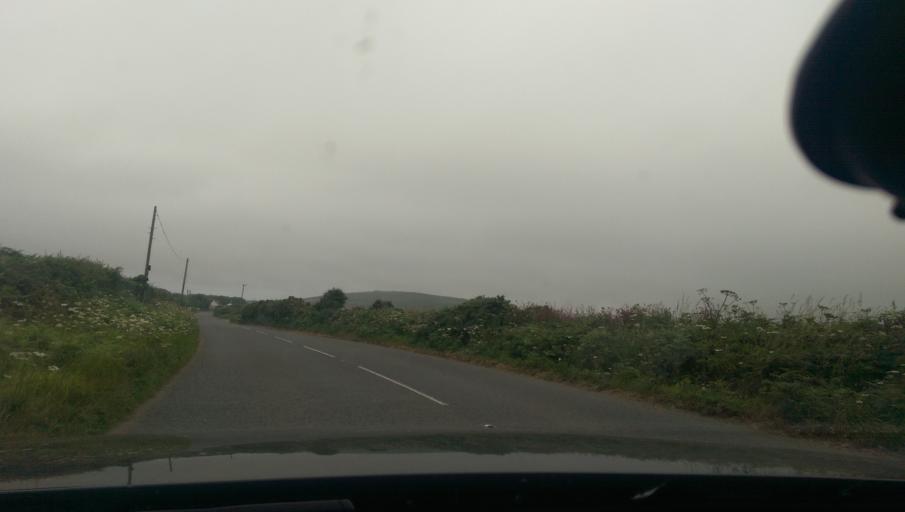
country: GB
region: England
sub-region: Cornwall
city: St. Buryan
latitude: 50.0912
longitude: -5.6370
